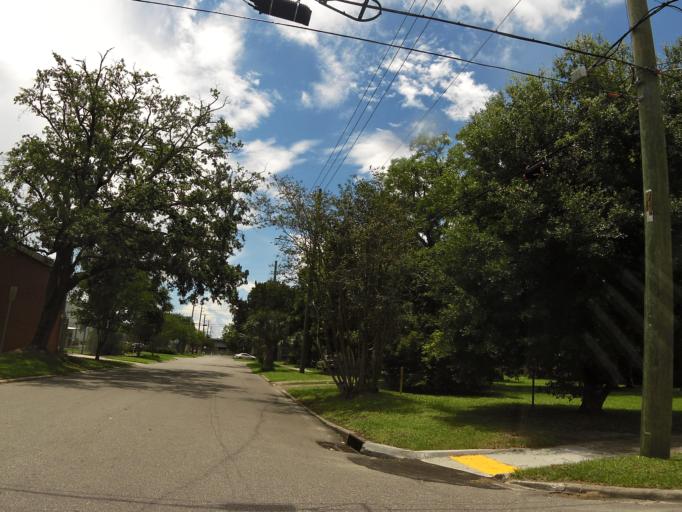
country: US
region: Florida
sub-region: Duval County
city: Jacksonville
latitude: 30.3543
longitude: -81.6476
